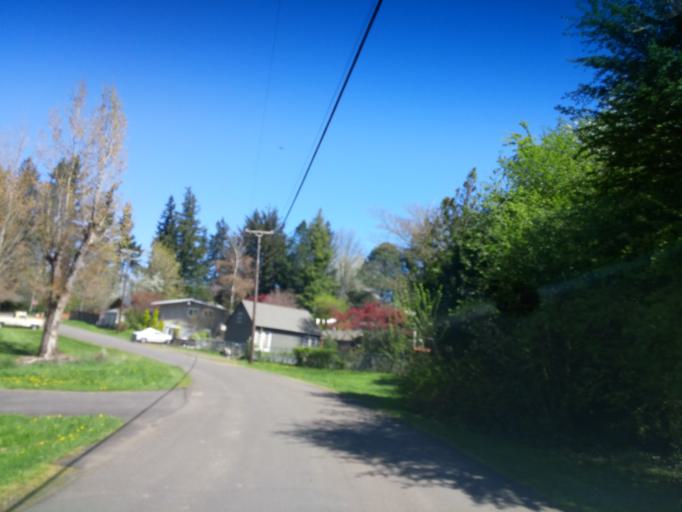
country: US
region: Oregon
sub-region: Washington County
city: West Haven
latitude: 45.5220
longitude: -122.7769
